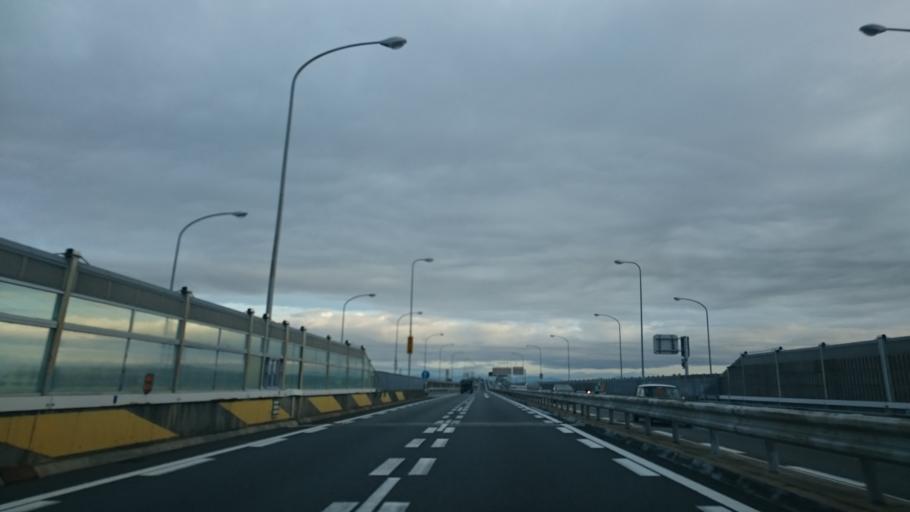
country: JP
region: Aichi
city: Kanie
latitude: 35.1642
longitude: 136.8172
